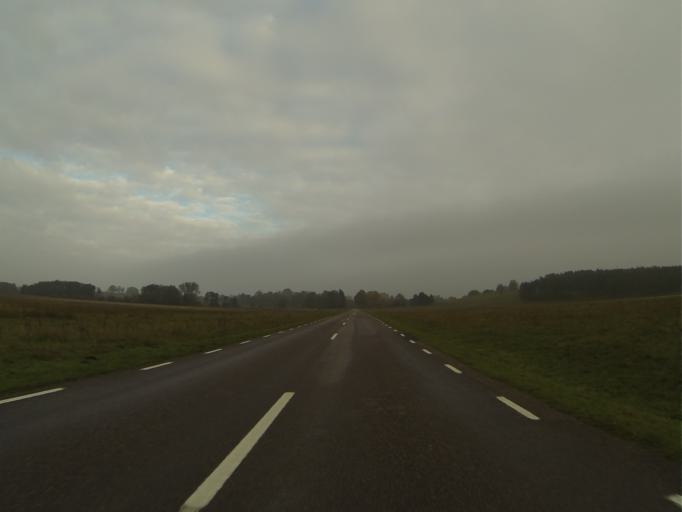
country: SE
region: Skane
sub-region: Lunds Kommun
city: Veberod
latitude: 55.6783
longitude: 13.4985
